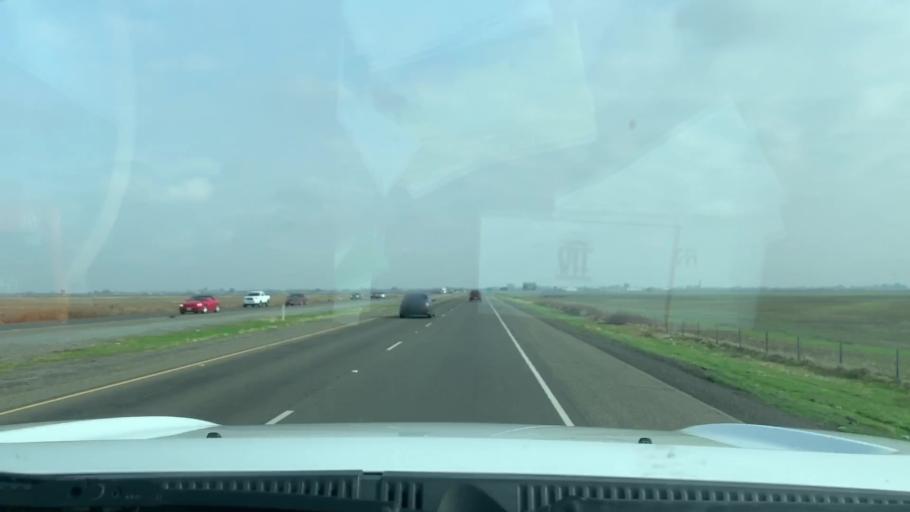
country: US
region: California
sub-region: Kings County
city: Lemoore
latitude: 36.2728
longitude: -119.8294
